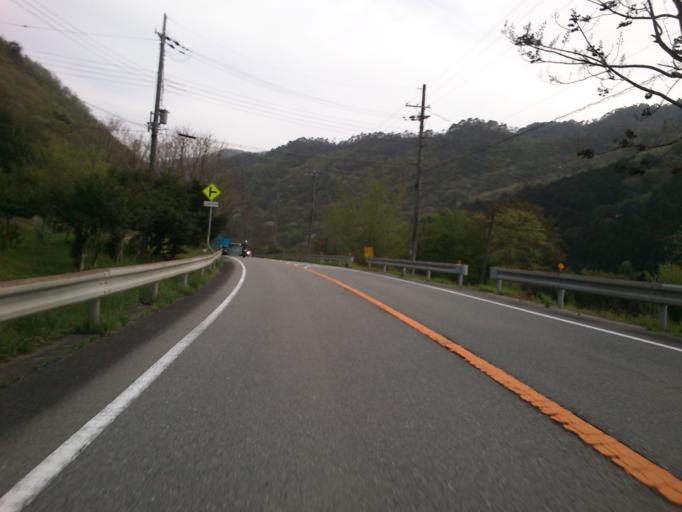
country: JP
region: Hyogo
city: Sasayama
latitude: 35.1389
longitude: 135.3335
